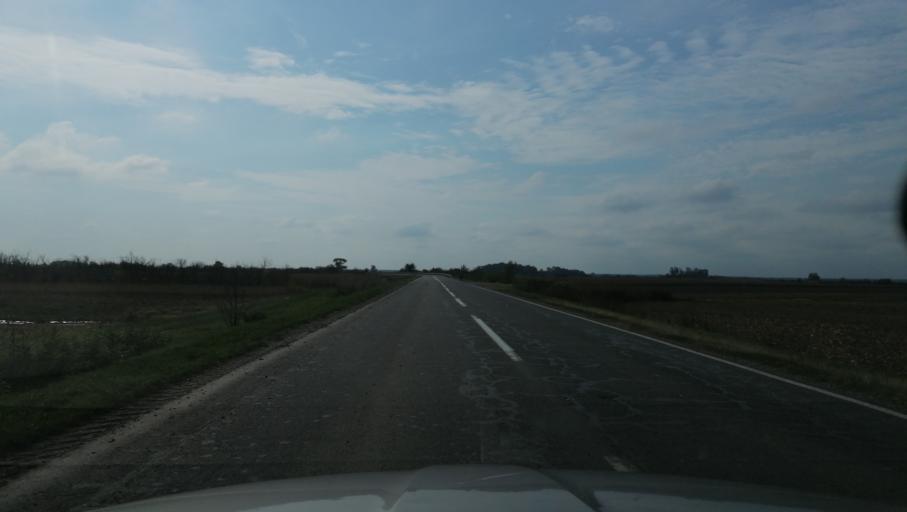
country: RS
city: Ravnje
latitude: 45.0064
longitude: 19.3897
